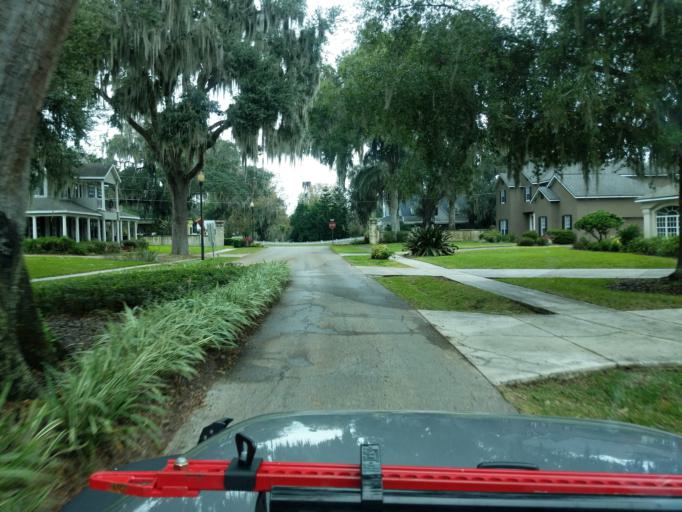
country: US
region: Florida
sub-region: Orange County
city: Oakland
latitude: 28.5600
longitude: -81.6273
